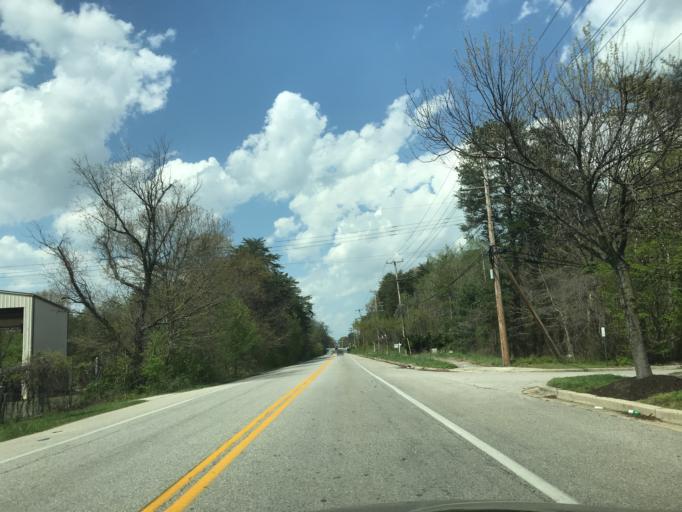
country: US
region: Maryland
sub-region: Anne Arundel County
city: Severn
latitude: 39.1583
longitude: -76.6681
